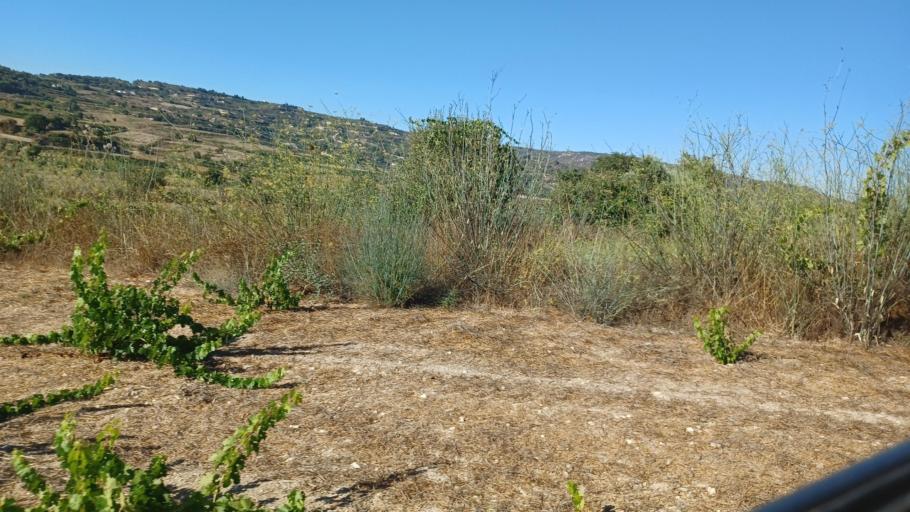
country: CY
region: Pafos
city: Mesogi
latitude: 34.8742
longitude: 32.5029
